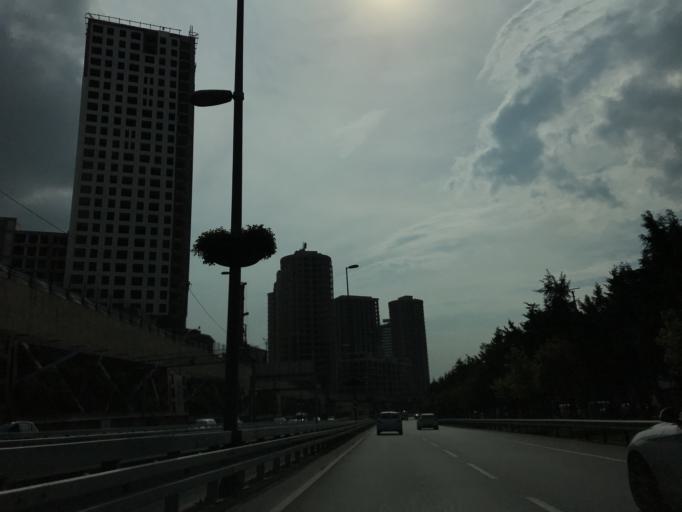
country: TR
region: Istanbul
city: UEskuedar
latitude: 40.9957
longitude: 29.0517
